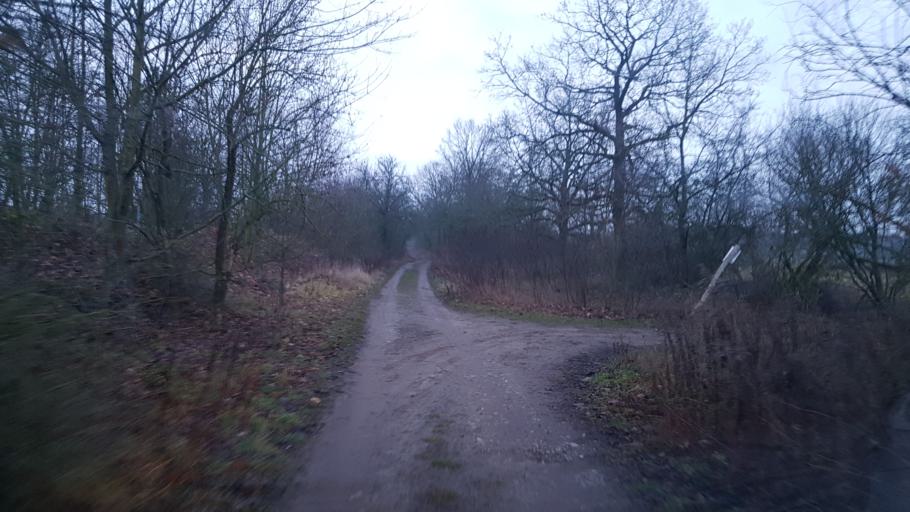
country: DE
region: Brandenburg
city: Stahnsdorf
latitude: 52.3619
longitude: 13.2013
